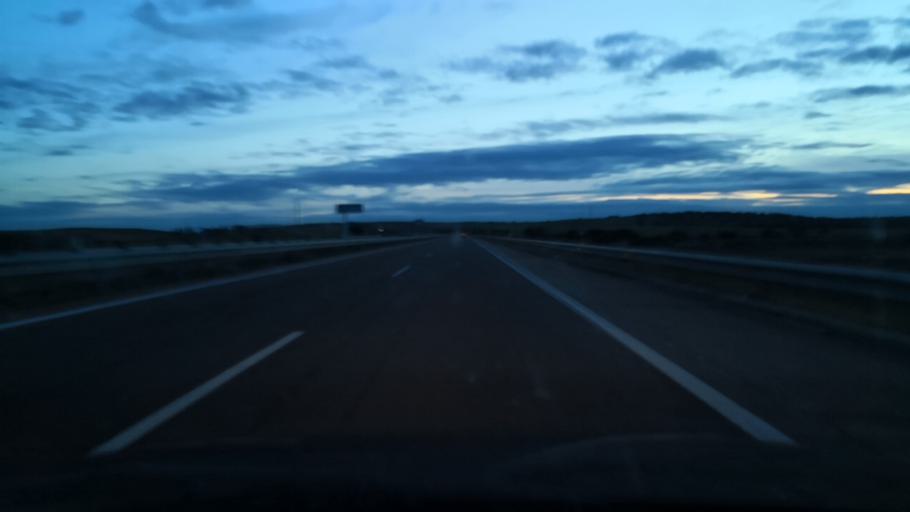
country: ES
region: Extremadura
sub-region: Provincia de Badajoz
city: Badajoz
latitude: 38.9191
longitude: -6.9731
